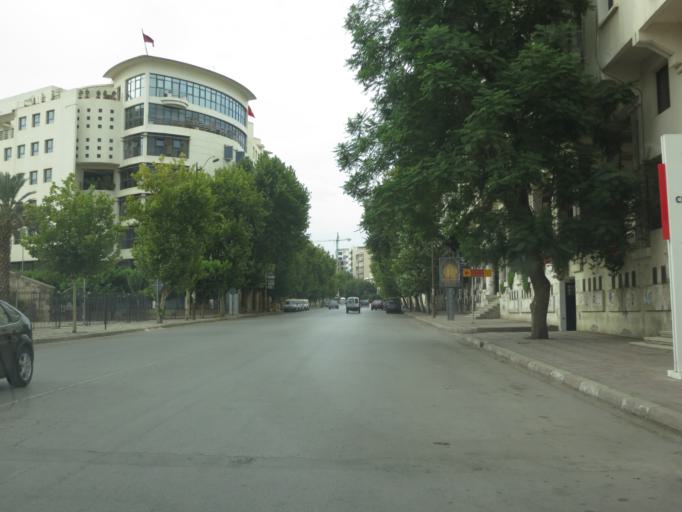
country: MA
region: Fes-Boulemane
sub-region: Fes
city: Fes
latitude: 34.0424
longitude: -5.0036
